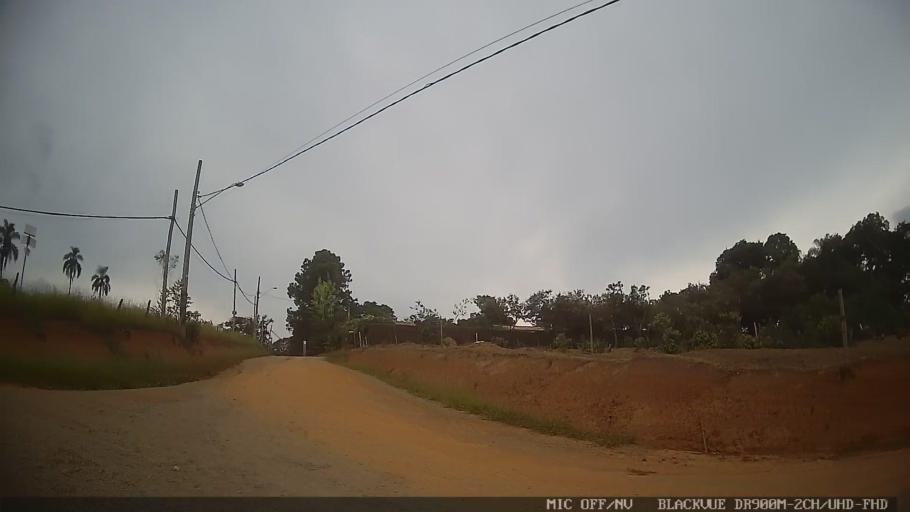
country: BR
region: Sao Paulo
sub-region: Atibaia
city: Atibaia
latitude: -23.1854
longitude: -46.6163
